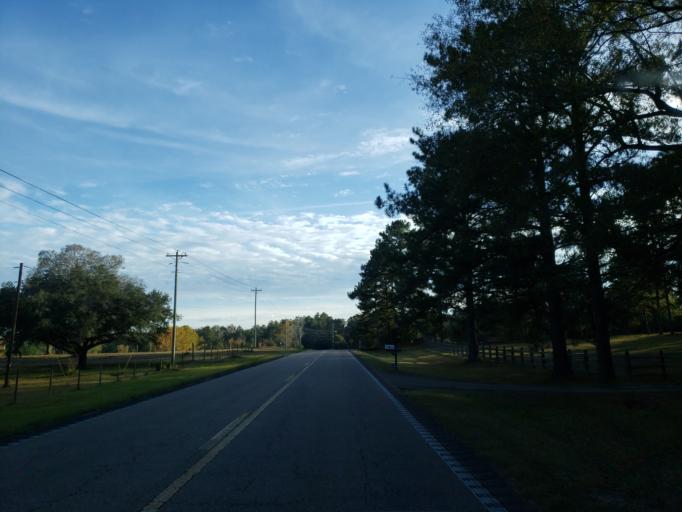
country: US
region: Mississippi
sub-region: Lamar County
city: West Hattiesburg
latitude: 31.2590
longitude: -89.4632
